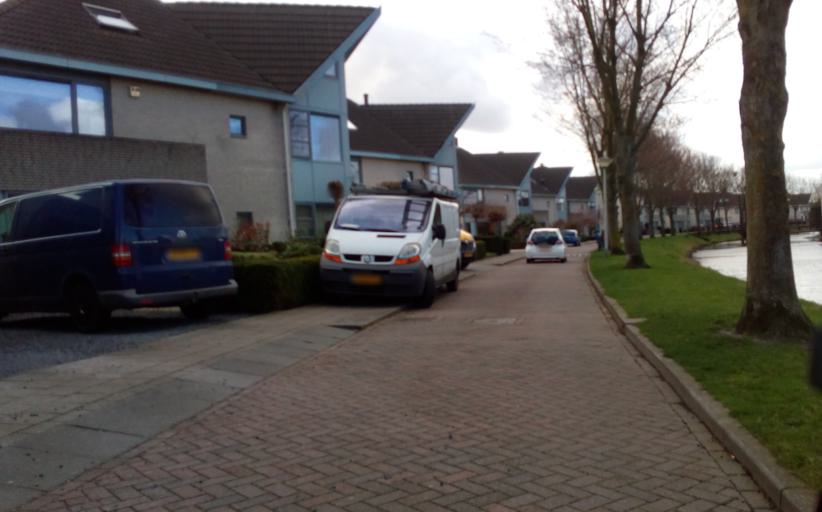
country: NL
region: South Holland
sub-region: Gemeente Lansingerland
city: Bergschenhoek
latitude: 51.9944
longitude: 4.5080
